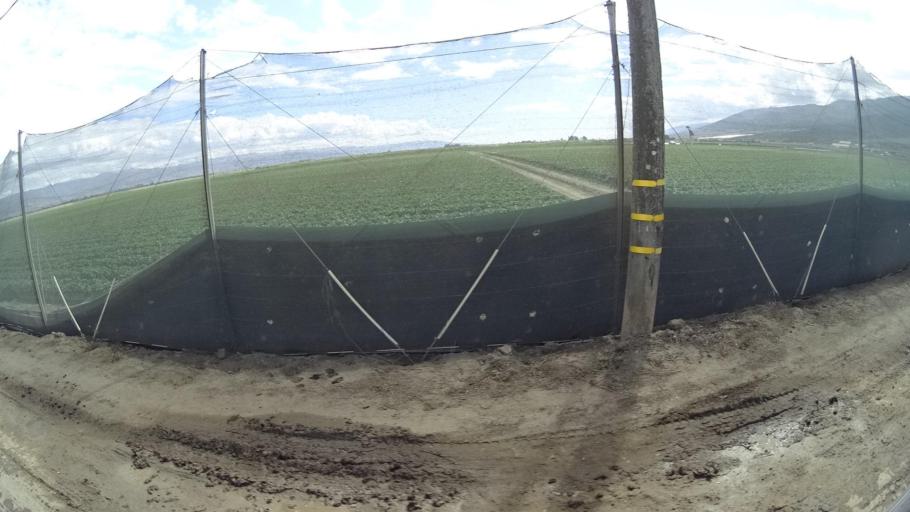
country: US
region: California
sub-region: Monterey County
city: Chualar
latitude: 36.6035
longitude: -121.6026
